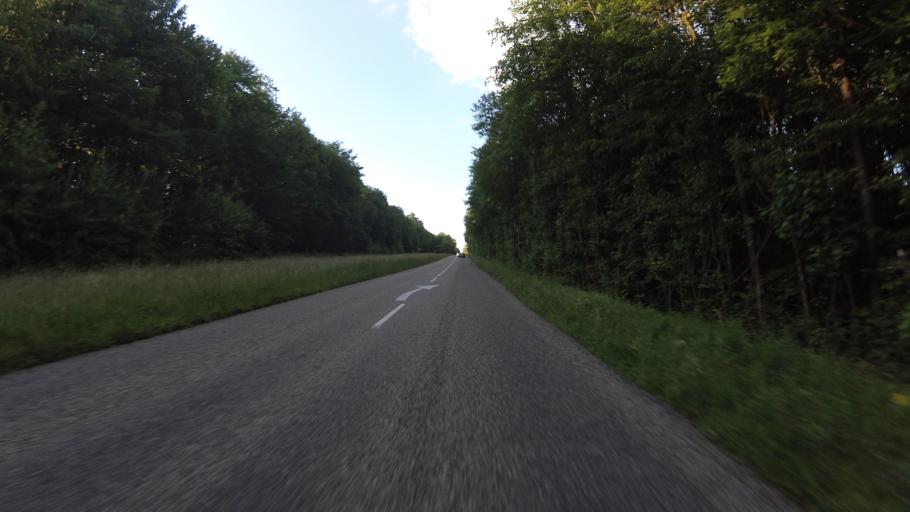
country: FR
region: Alsace
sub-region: Departement du Bas-Rhin
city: Herbitzheim
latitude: 49.0296
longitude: 7.0812
